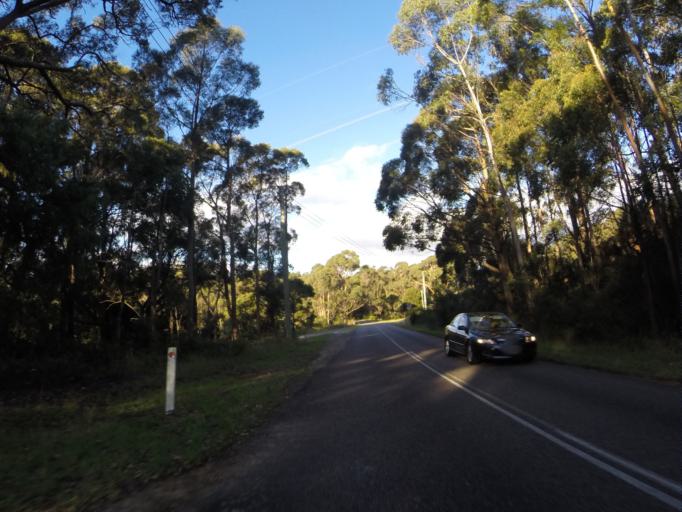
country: AU
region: New South Wales
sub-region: Shoalhaven Shire
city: Kangaroo Valley
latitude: -34.6468
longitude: 150.5077
